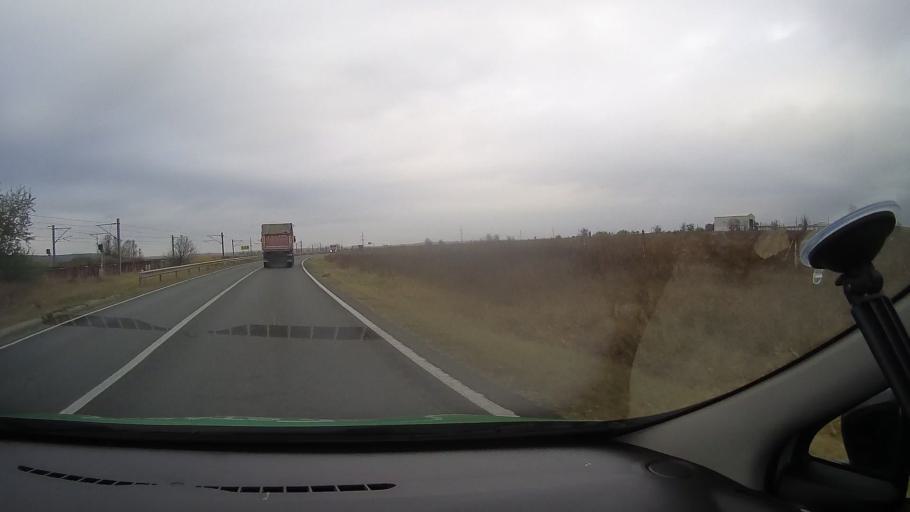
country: RO
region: Constanta
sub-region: Comuna Poarta Alba
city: Poarta Alba
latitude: 44.2294
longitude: 28.3792
